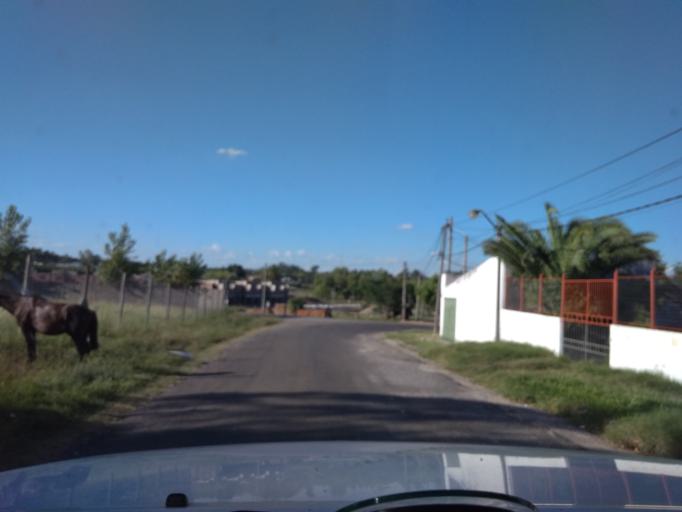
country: UY
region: Florida
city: Florida
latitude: -34.0974
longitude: -56.2270
